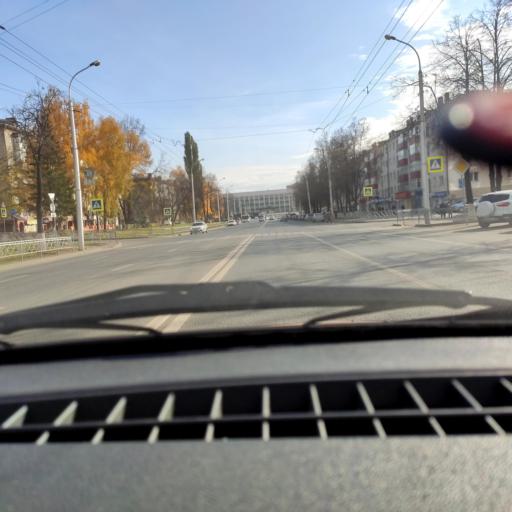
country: RU
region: Bashkortostan
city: Ufa
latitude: 54.8078
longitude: 56.1091
